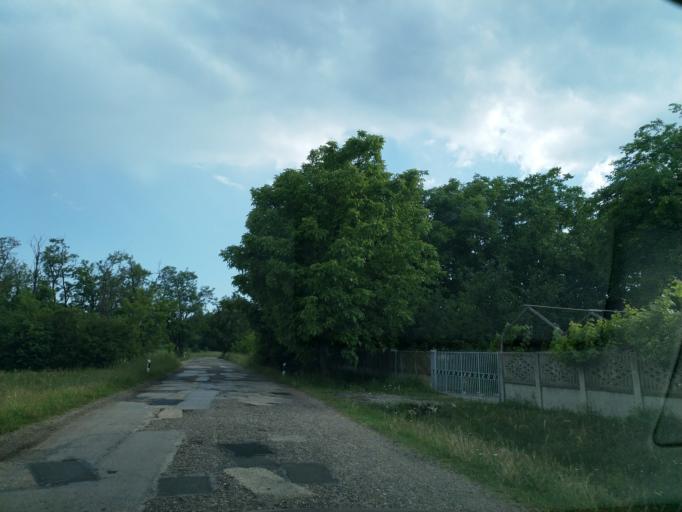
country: RS
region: Central Serbia
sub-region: Zajecarski Okrug
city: Boljevac
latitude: 43.9818
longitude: 21.9733
